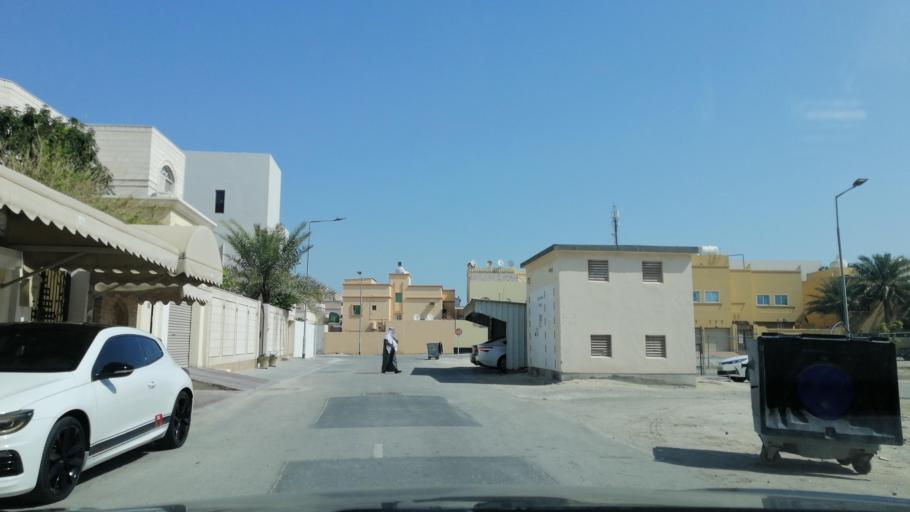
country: BH
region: Muharraq
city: Al Hadd
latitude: 26.2473
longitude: 50.6344
